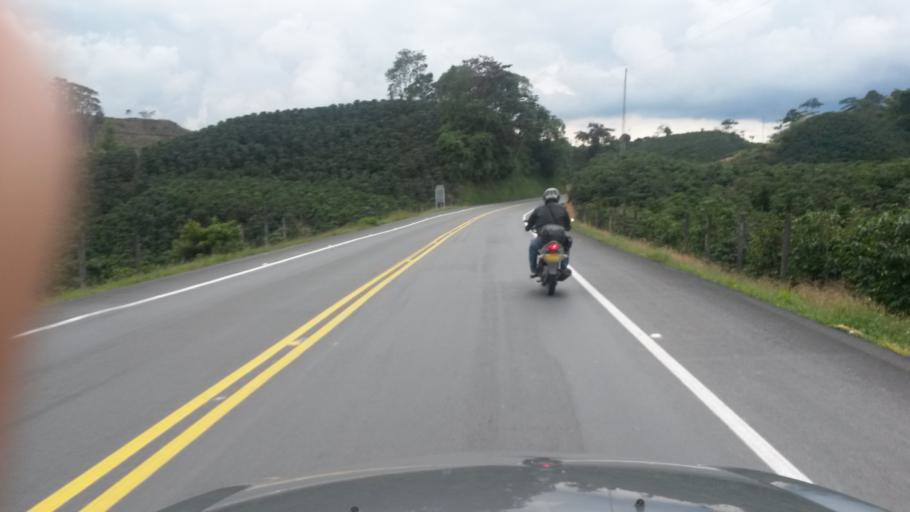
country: CO
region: Caldas
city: Chinchina
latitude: 4.9785
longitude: -75.6178
